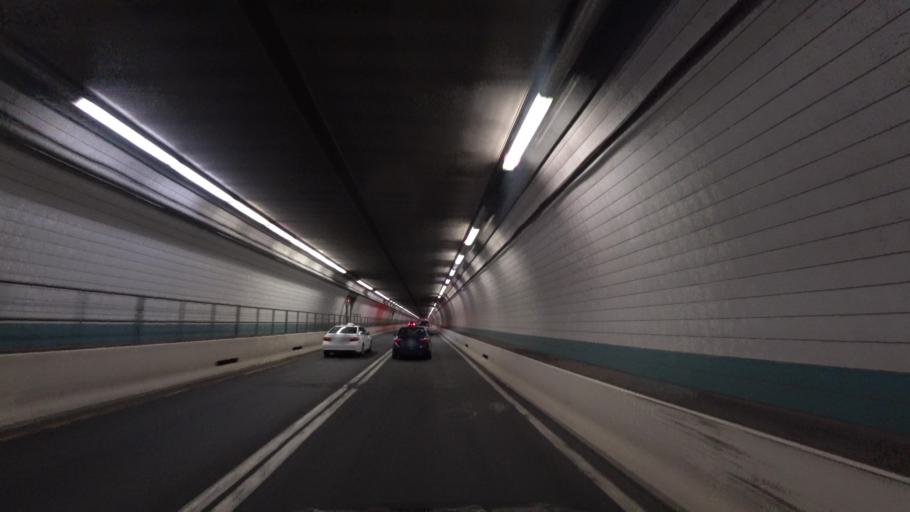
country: US
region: Massachusetts
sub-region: Suffolk County
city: South Boston
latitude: 42.3534
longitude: -71.0303
